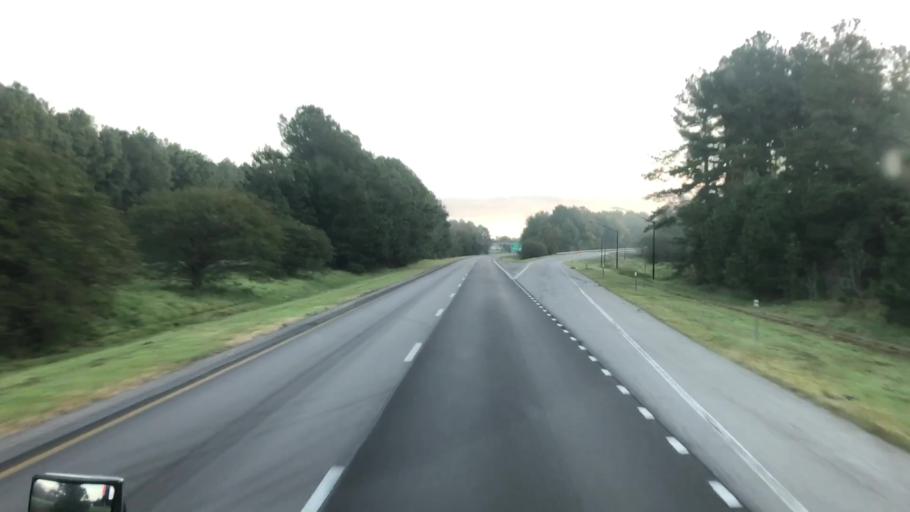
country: US
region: South Carolina
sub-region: Clarendon County
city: Manning
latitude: 33.5861
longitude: -80.3615
